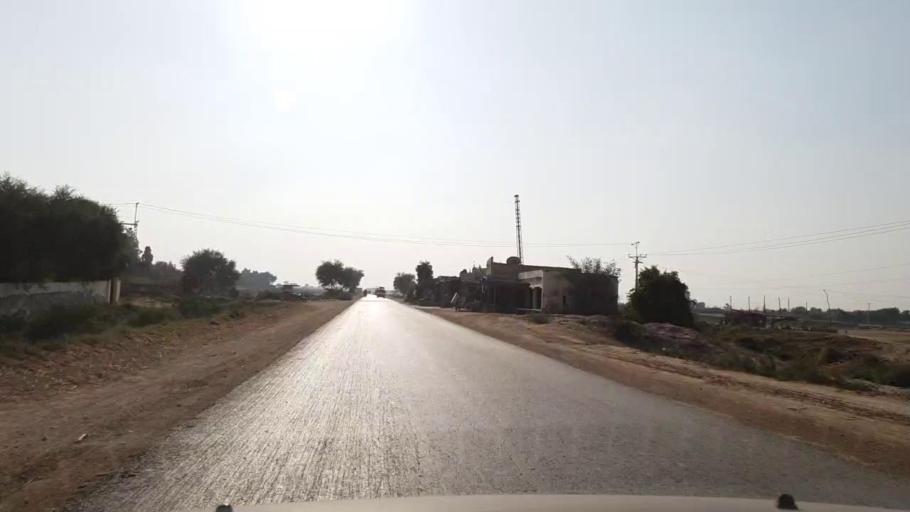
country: PK
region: Sindh
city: Tando Muhammad Khan
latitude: 25.0263
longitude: 68.4199
